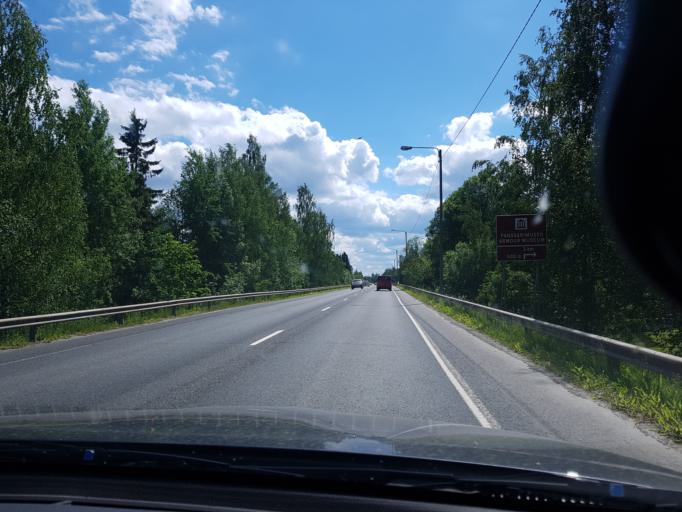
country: FI
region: Haeme
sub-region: Haemeenlinna
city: Parola
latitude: 61.0648
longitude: 24.3924
